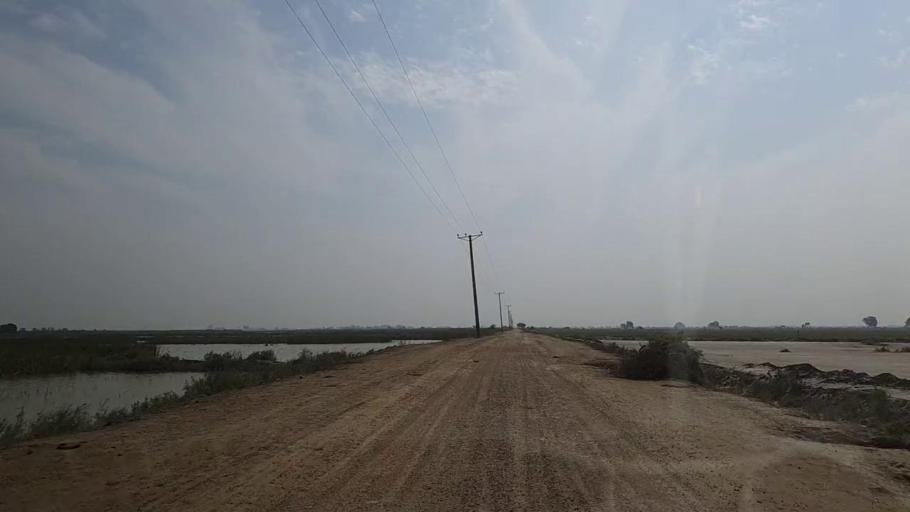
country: PK
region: Sindh
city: Mirpur Batoro
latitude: 24.6072
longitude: 68.2099
